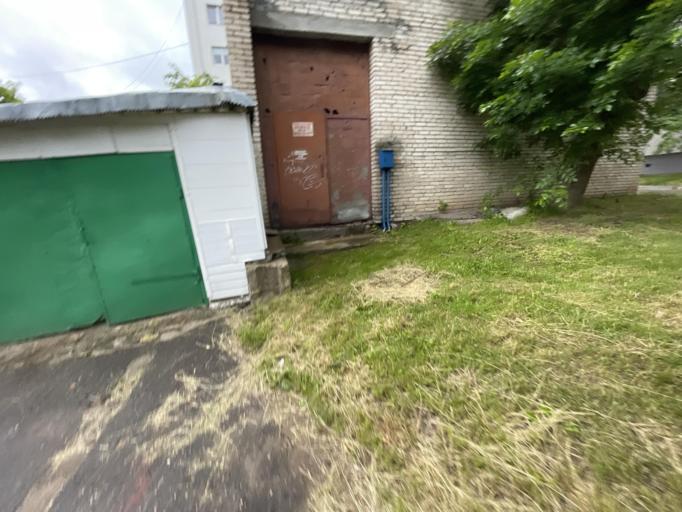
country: BY
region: Grodnenskaya
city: Hrodna
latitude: 53.6910
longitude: 23.8217
